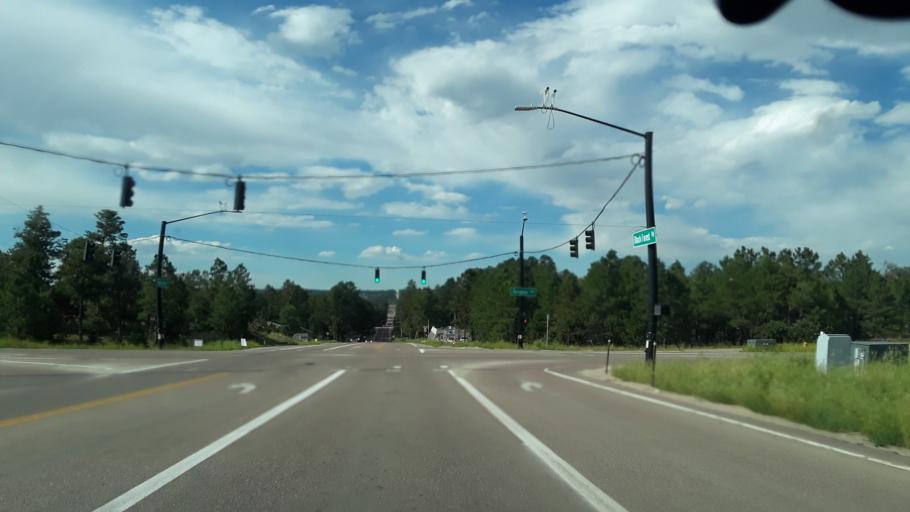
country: US
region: Colorado
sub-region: El Paso County
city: Black Forest
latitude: 38.9980
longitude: -104.7003
